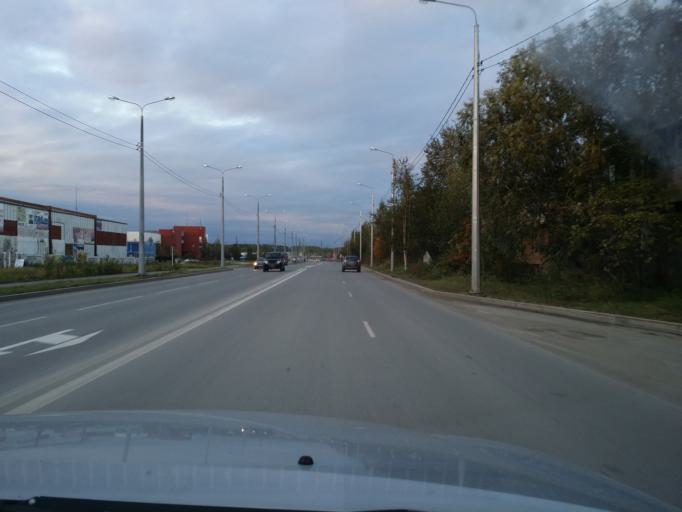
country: RU
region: Khanty-Mansiyskiy Avtonomnyy Okrug
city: Megion
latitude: 61.0382
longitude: 76.0993
